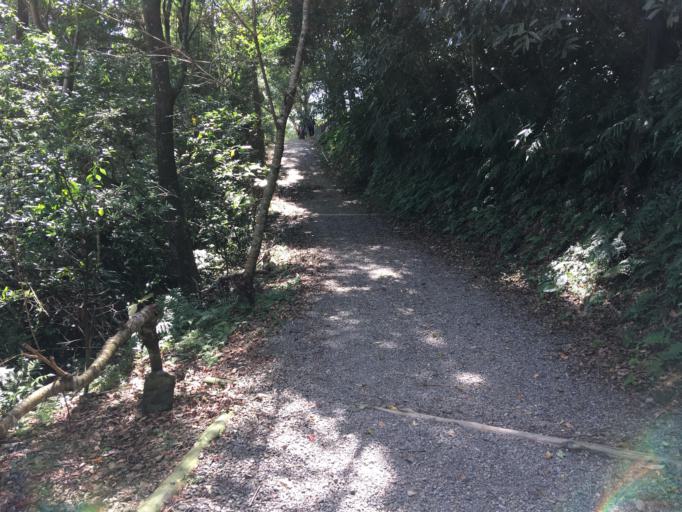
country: TW
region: Taiwan
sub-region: Yilan
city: Yilan
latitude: 24.8418
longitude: 121.7764
